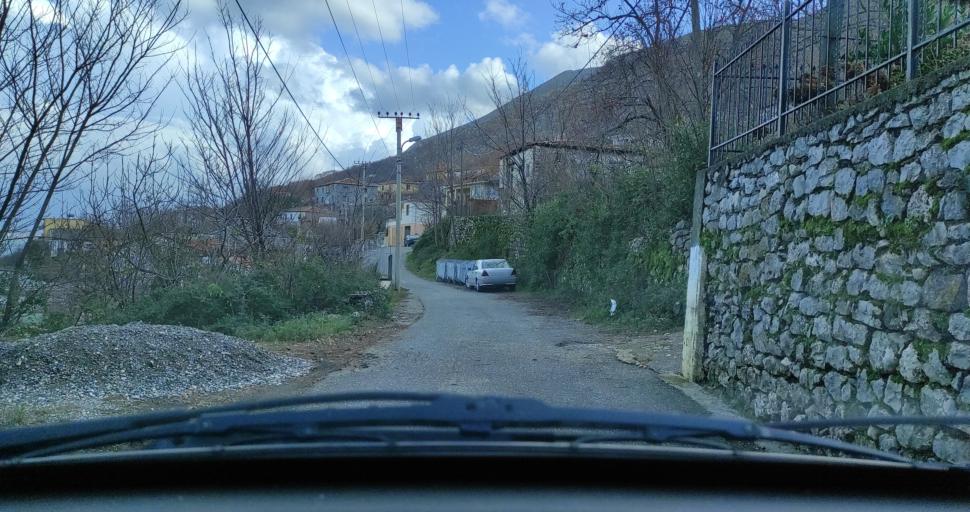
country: AL
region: Shkoder
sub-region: Rrethi i Shkodres
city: Dajc
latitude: 42.0714
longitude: 19.3990
